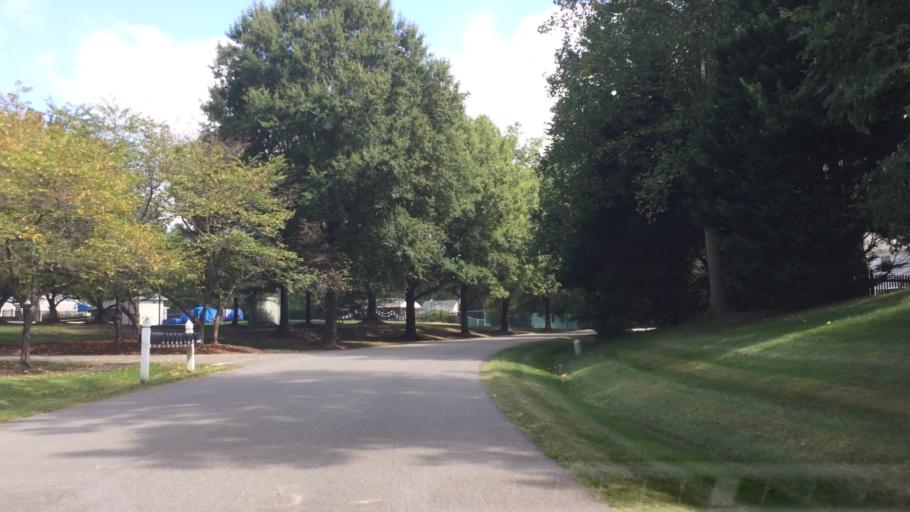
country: US
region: Virginia
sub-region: Henrico County
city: Chamberlayne
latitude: 37.6875
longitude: -77.4312
